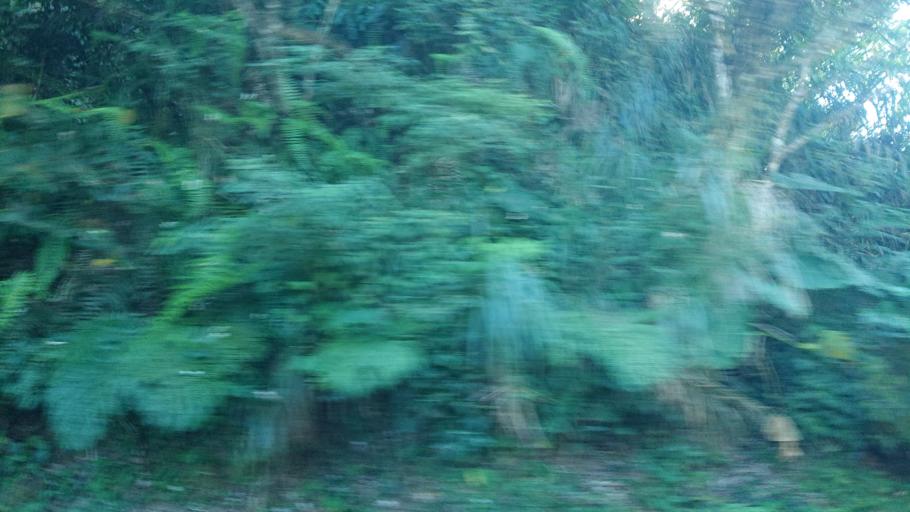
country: TW
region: Taiwan
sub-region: Chiayi
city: Jiayi Shi
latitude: 23.5336
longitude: 120.6292
